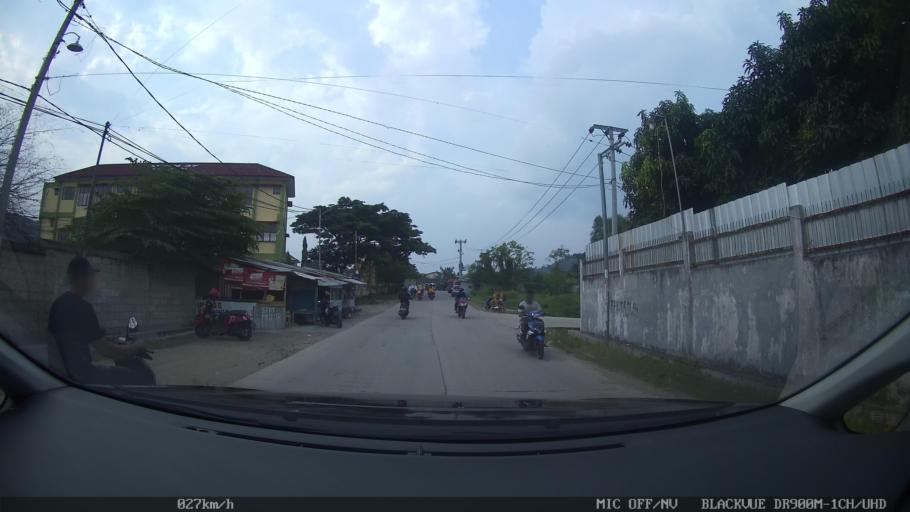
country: ID
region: Lampung
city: Bandarlampung
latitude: -5.4366
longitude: 105.2961
